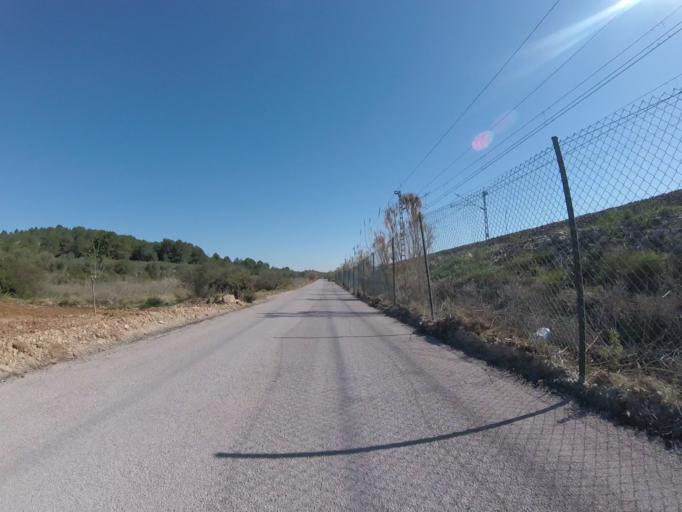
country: ES
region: Valencia
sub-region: Provincia de Castello
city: Santa Magdalena de Pulpis
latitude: 40.3437
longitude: 0.2673
